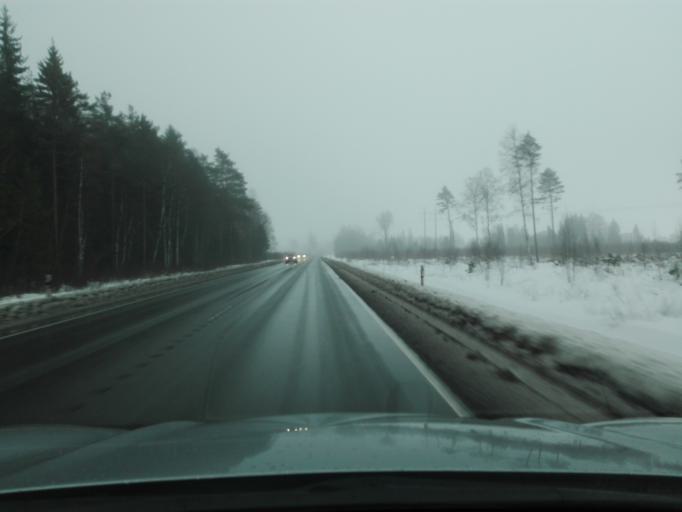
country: EE
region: Raplamaa
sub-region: Kohila vald
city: Kohila
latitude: 59.2363
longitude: 24.7652
